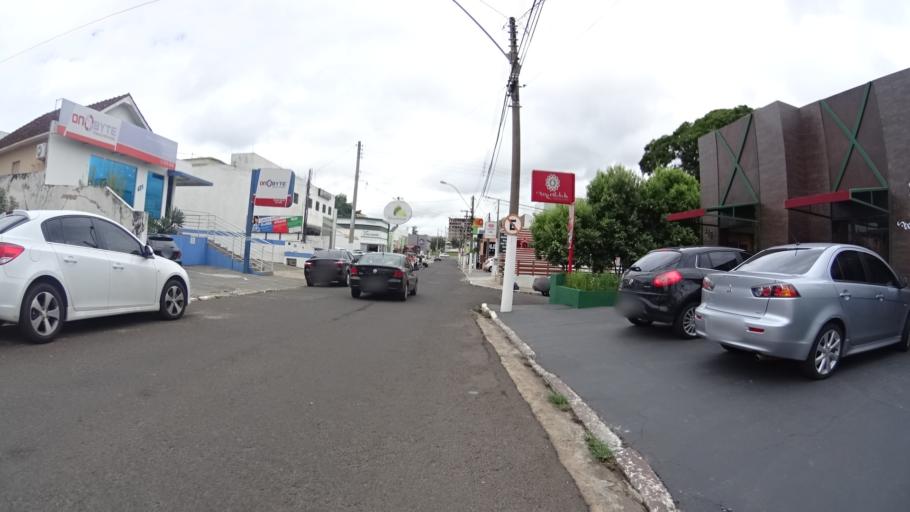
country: BR
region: Sao Paulo
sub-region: Marilia
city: Marilia
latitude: -22.2204
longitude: -49.9439
